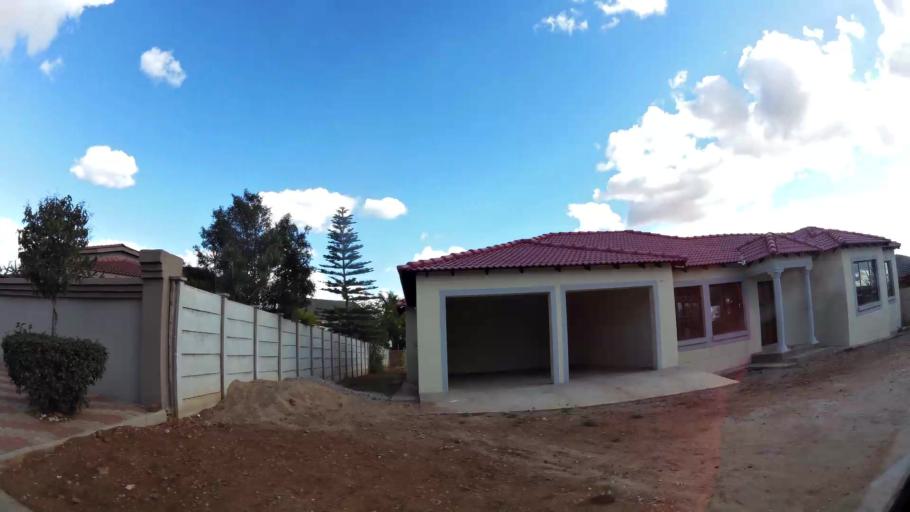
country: ZA
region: Limpopo
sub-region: Capricorn District Municipality
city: Polokwane
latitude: -23.9107
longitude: 29.5022
